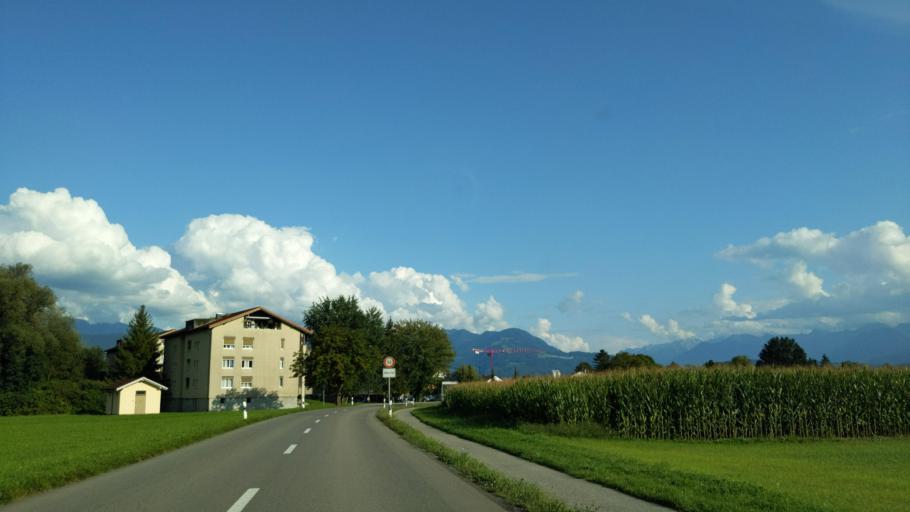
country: CH
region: Saint Gallen
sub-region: Wahlkreis Rheintal
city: Oberriet
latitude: 47.3288
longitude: 9.5619
